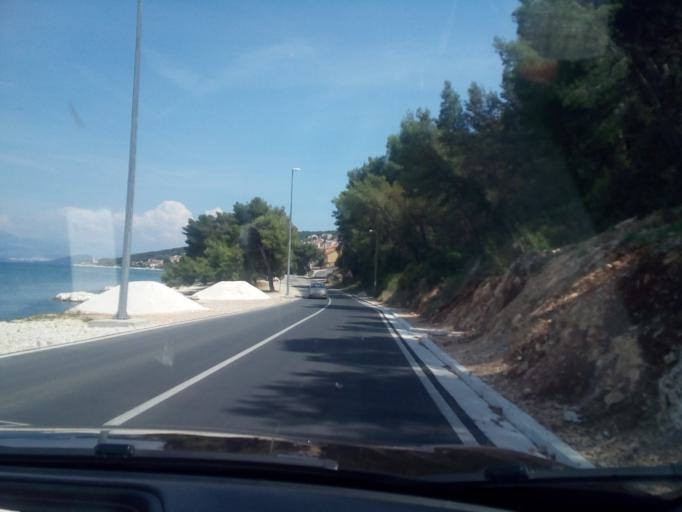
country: HR
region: Splitsko-Dalmatinska
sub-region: Grad Trogir
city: Trogir
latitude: 43.5153
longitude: 16.2725
